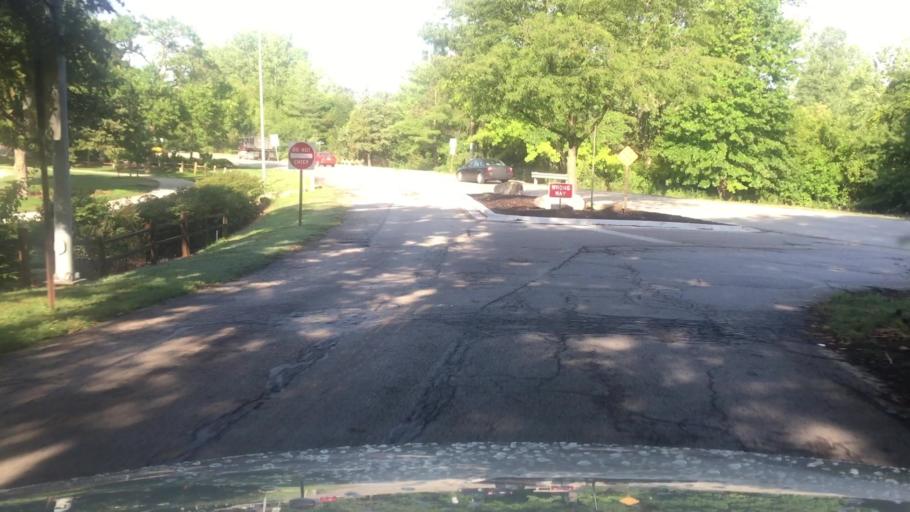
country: US
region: Kansas
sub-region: Johnson County
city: Shawnee
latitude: 39.0508
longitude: -94.7684
